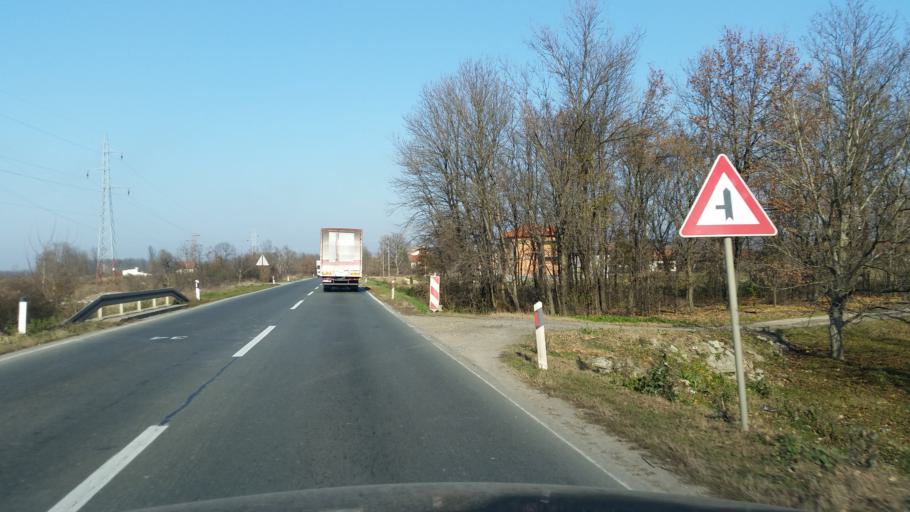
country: RS
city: Stepojevac
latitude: 44.4696
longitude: 20.2756
